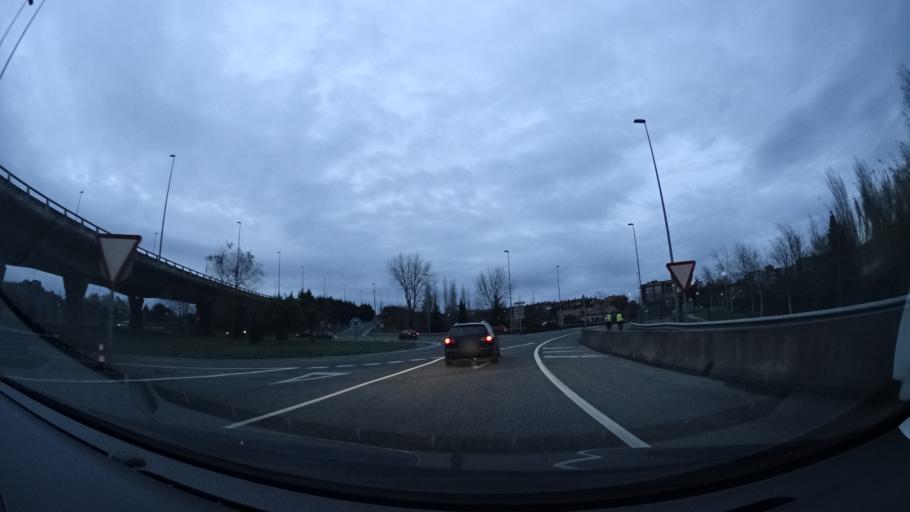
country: ES
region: Basque Country
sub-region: Bizkaia
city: Berango
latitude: 43.3627
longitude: -3.0019
